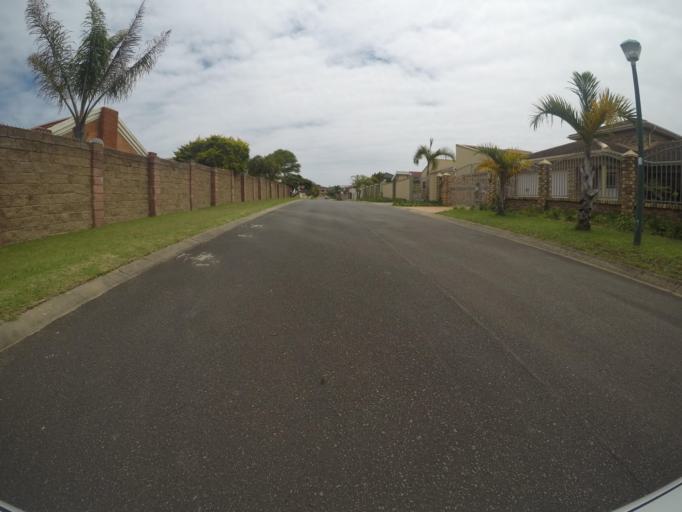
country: ZA
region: Eastern Cape
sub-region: Buffalo City Metropolitan Municipality
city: East London
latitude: -32.9779
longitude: 27.9560
